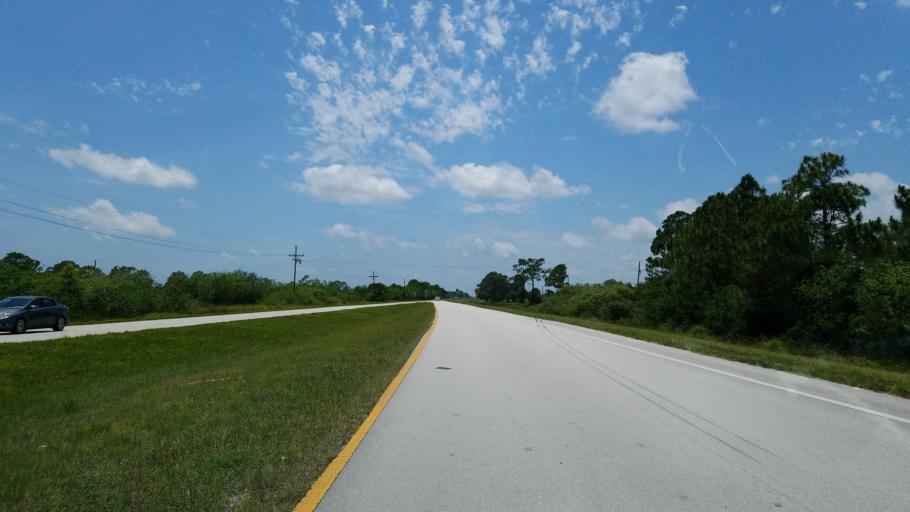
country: US
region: Florida
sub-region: Martin County
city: Palm City
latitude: 27.1617
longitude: -80.3987
